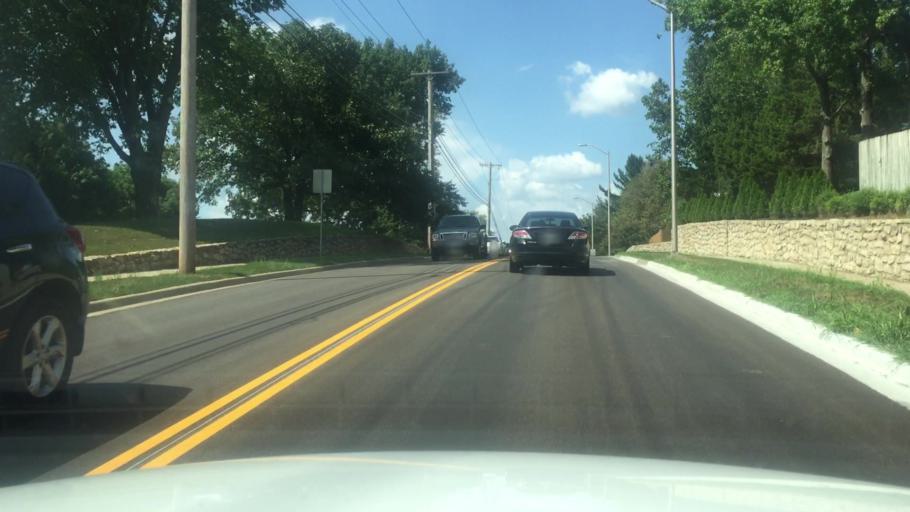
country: US
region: Kansas
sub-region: Johnson County
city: Lenexa
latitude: 38.9830
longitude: -94.7423
